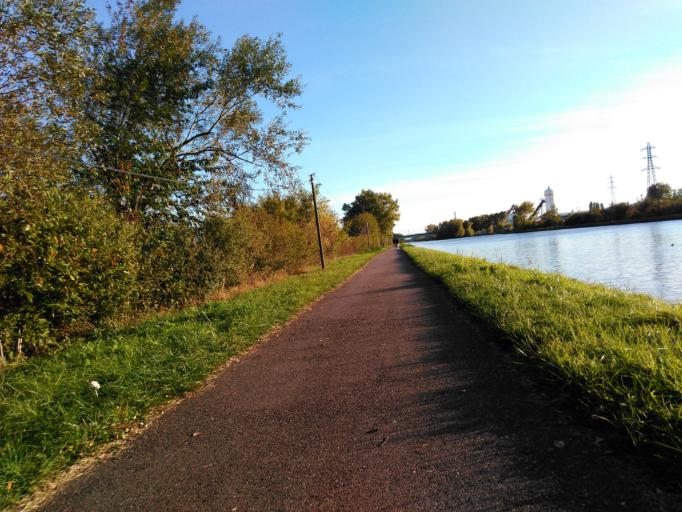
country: FR
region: Lorraine
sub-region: Departement de la Moselle
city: Talange
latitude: 49.2241
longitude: 6.1833
